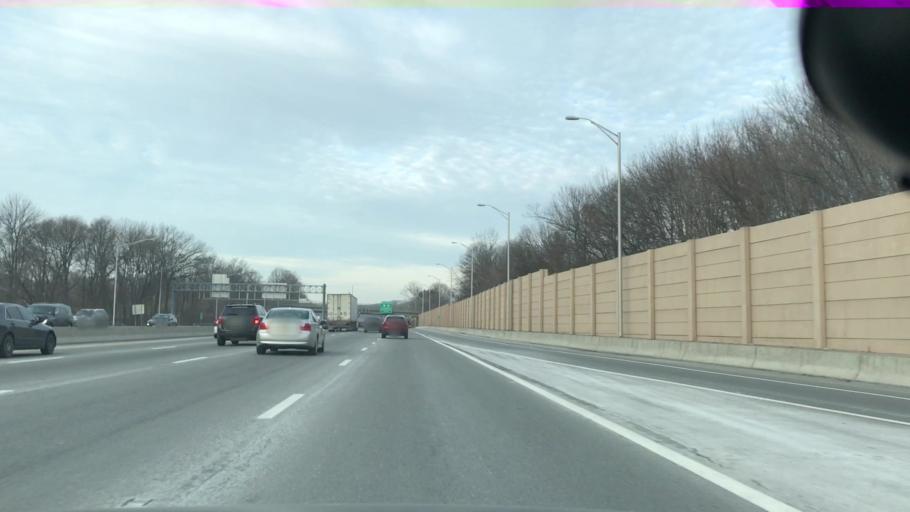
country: US
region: New Jersey
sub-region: Morris County
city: Parsippany
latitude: 40.8647
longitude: -74.4194
